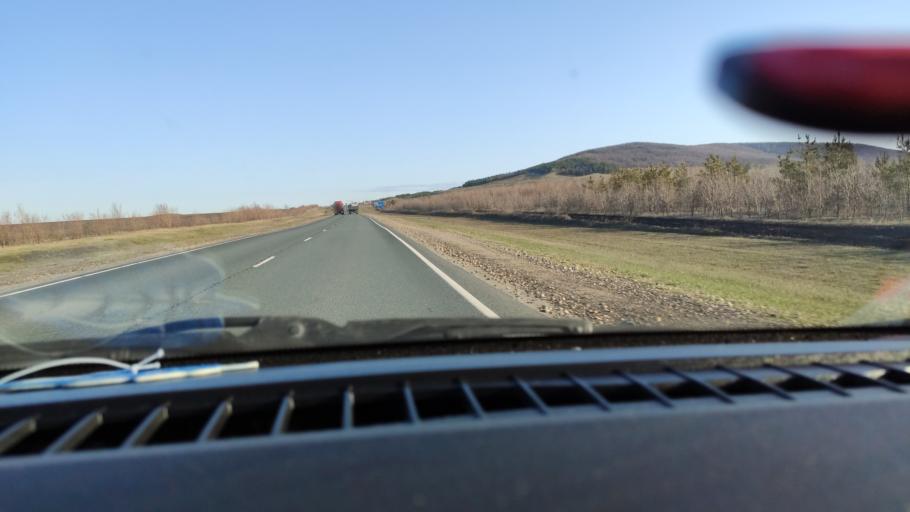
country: RU
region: Saratov
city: Alekseyevka
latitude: 52.2848
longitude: 47.9316
